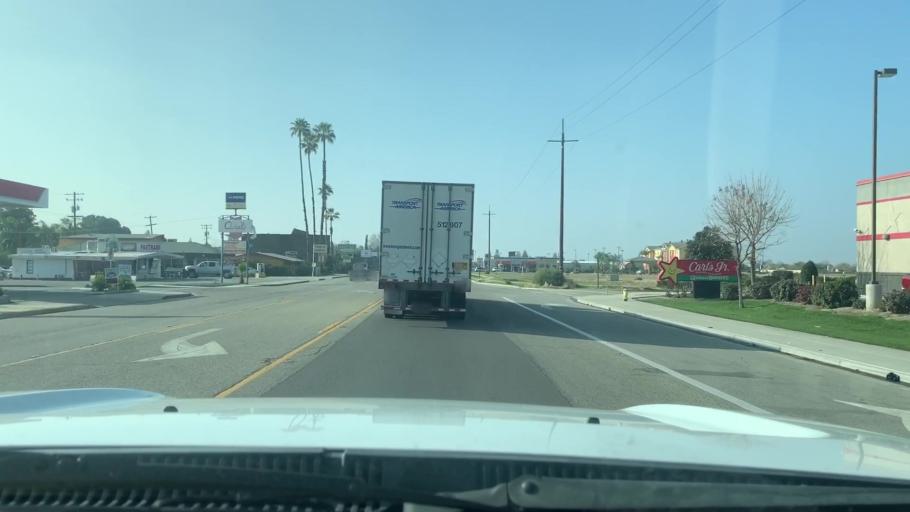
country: US
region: California
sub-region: Kern County
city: Wasco
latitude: 35.6016
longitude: -119.3420
